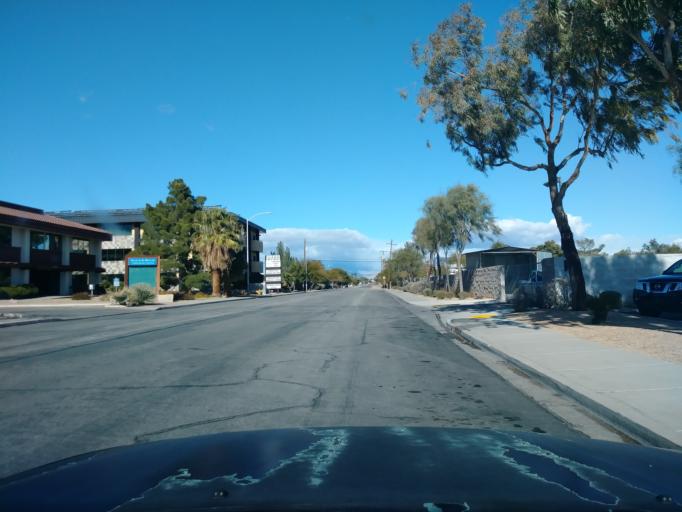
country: US
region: Nevada
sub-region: Clark County
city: Spring Valley
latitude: 36.1450
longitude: -115.2231
